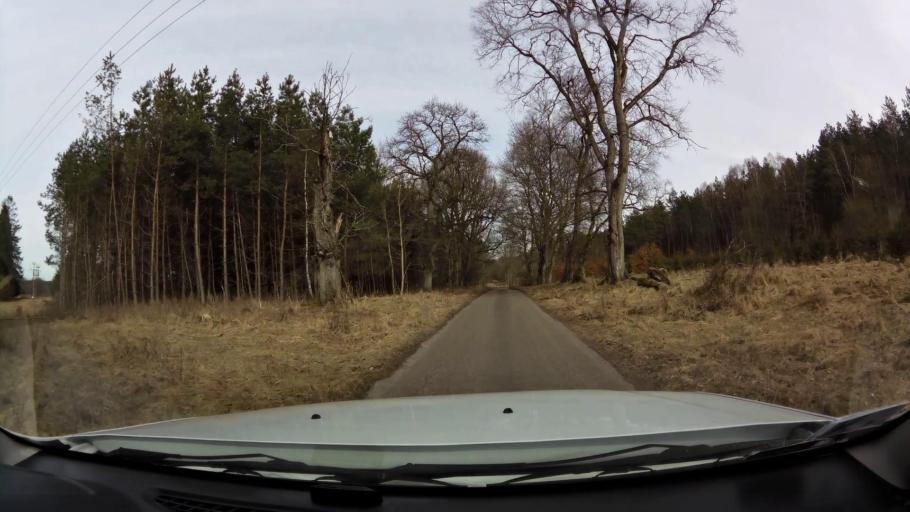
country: PL
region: West Pomeranian Voivodeship
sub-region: Powiat drawski
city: Drawsko Pomorskie
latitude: 53.4725
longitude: 15.6982
